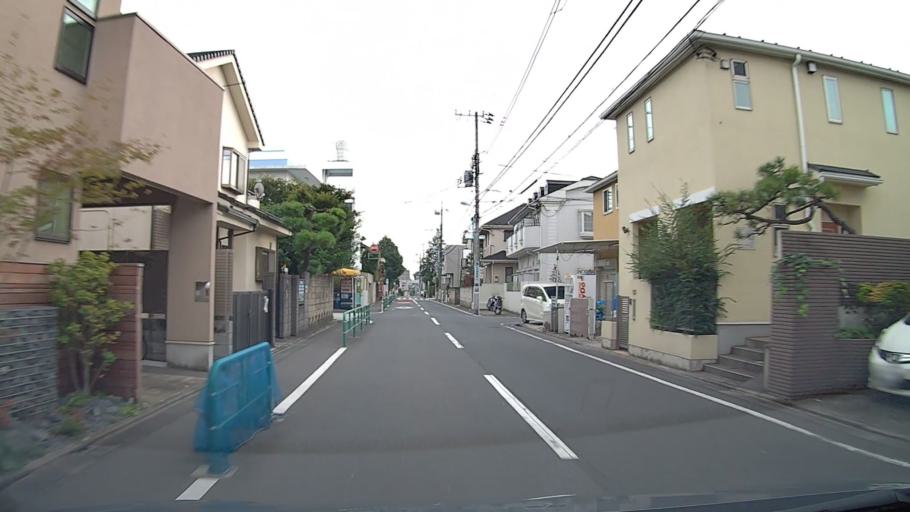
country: JP
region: Tokyo
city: Musashino
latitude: 35.7083
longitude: 139.6109
